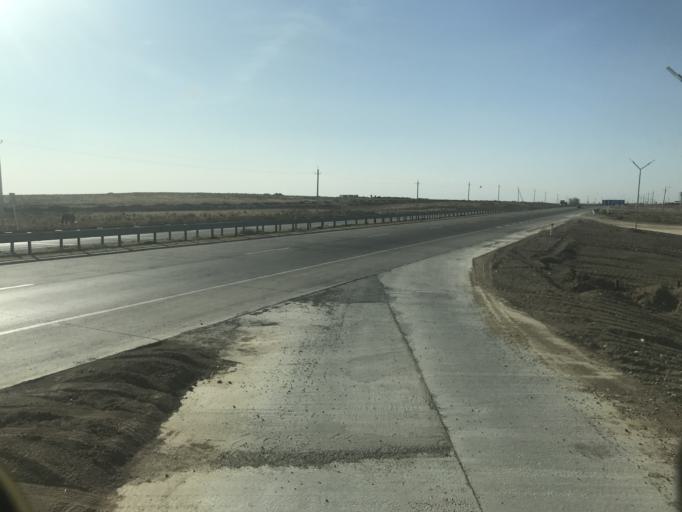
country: KZ
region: Ongtustik Qazaqstan
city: Shymkent
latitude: 42.4574
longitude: 69.6000
